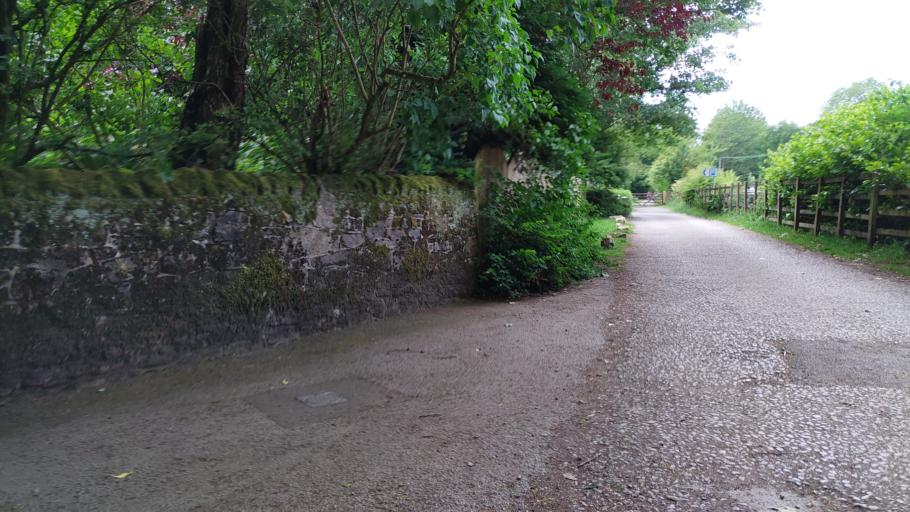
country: GB
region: England
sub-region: Lancashire
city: Clayton-le-Woods
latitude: 53.6900
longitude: -2.6435
